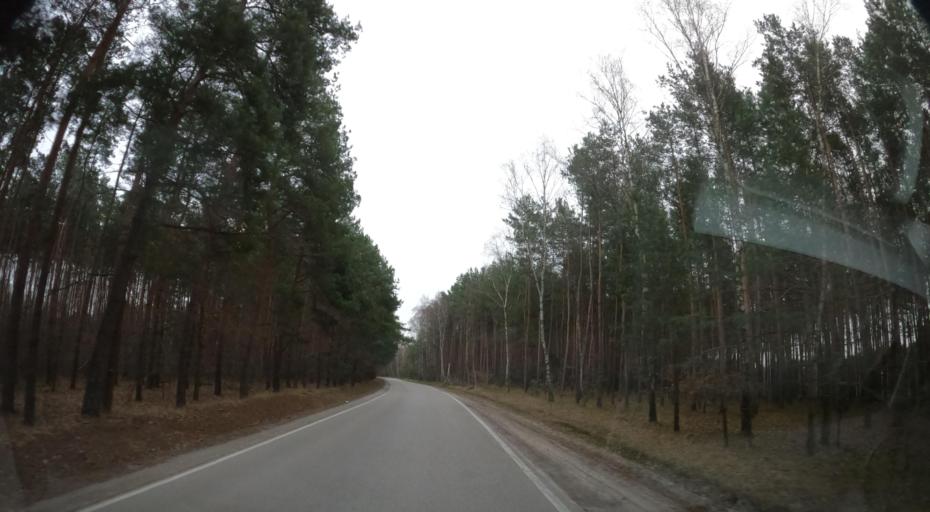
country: PL
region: Masovian Voivodeship
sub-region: Powiat radomski
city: Jedlinsk
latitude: 51.4898
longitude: 21.1661
